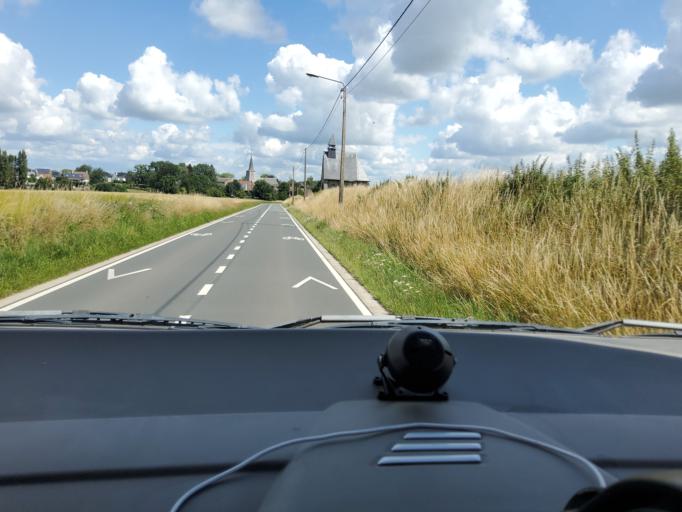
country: BE
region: Wallonia
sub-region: Province du Hainaut
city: Fleurus
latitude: 50.4997
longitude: 4.5497
